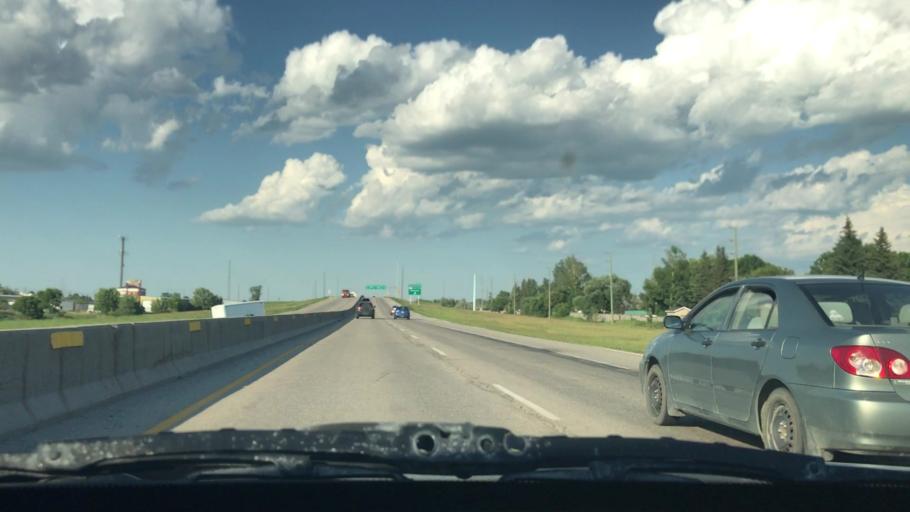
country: CA
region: Manitoba
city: Winnipeg
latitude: 49.7734
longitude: -97.1673
